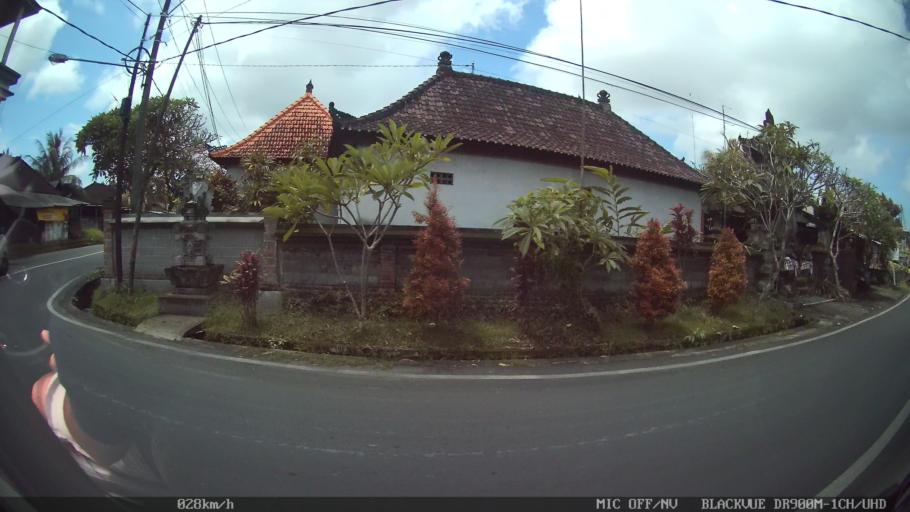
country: ID
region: Bali
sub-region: Kabupaten Gianyar
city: Ubud
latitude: -8.5308
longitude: 115.2824
